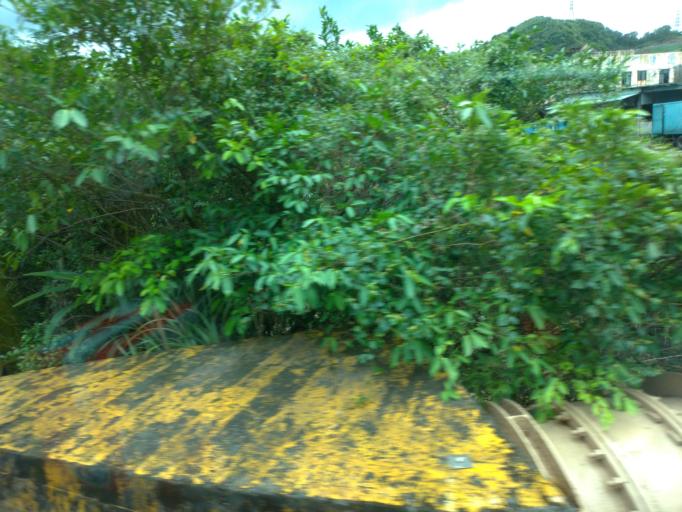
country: TW
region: Taiwan
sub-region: Keelung
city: Keelung
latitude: 25.1139
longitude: 121.7291
